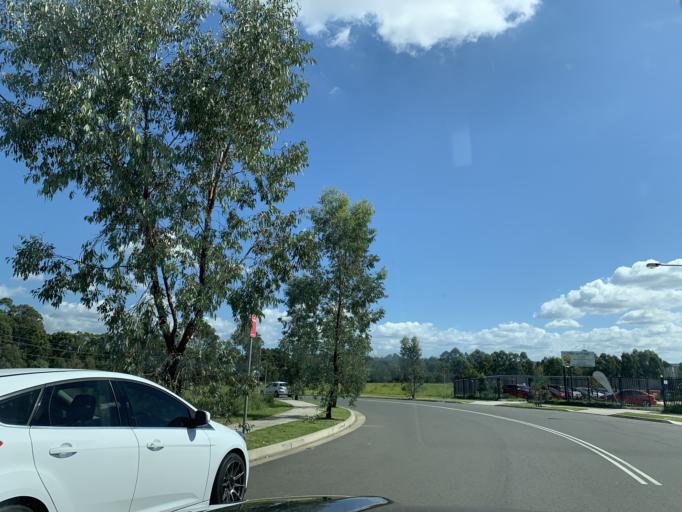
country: AU
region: New South Wales
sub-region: Penrith Municipality
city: Penrith
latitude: -33.7301
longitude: 150.7034
